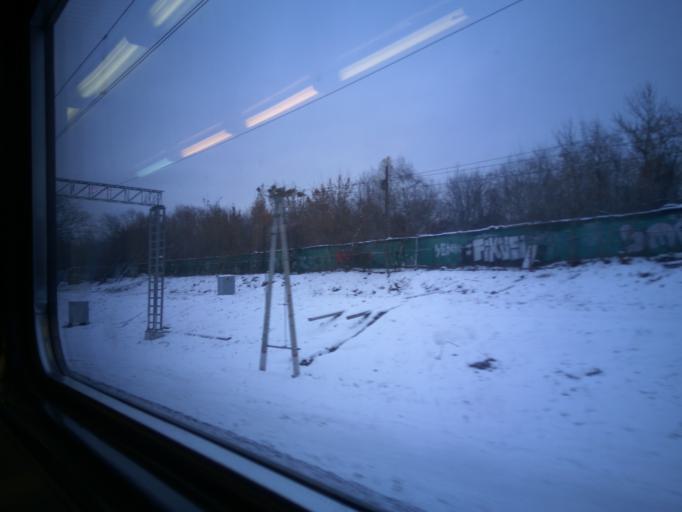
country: RU
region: Moskovskaya
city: Kastanayevo
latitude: 55.7343
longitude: 37.4971
